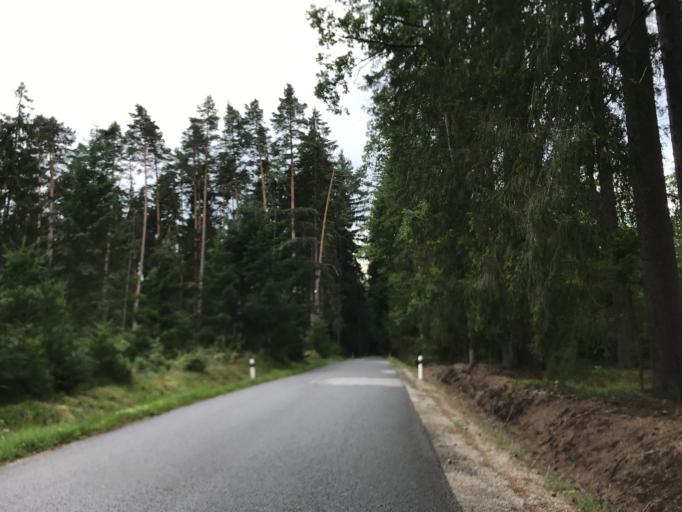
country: CZ
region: Jihocesky
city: Suchdol nad Luznici
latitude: 48.9373
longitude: 14.8519
